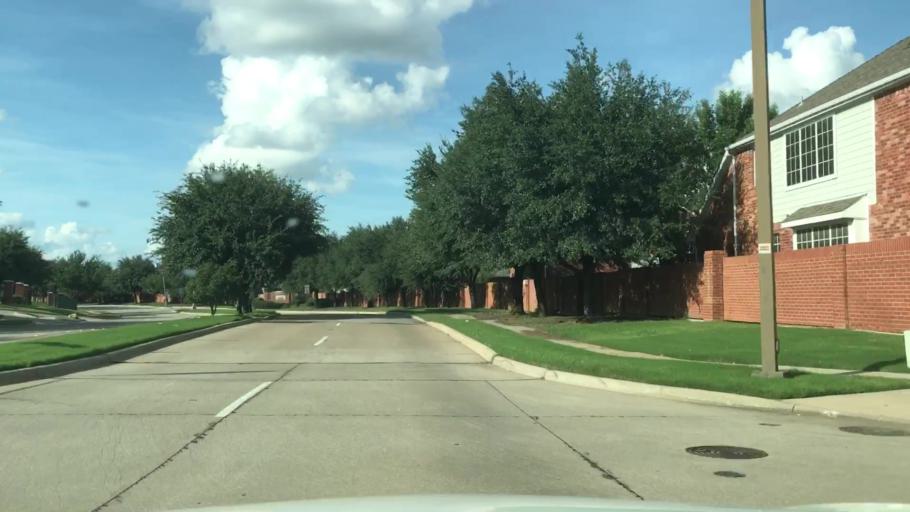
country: US
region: Texas
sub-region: Dallas County
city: Farmers Branch
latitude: 32.9273
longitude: -96.9579
